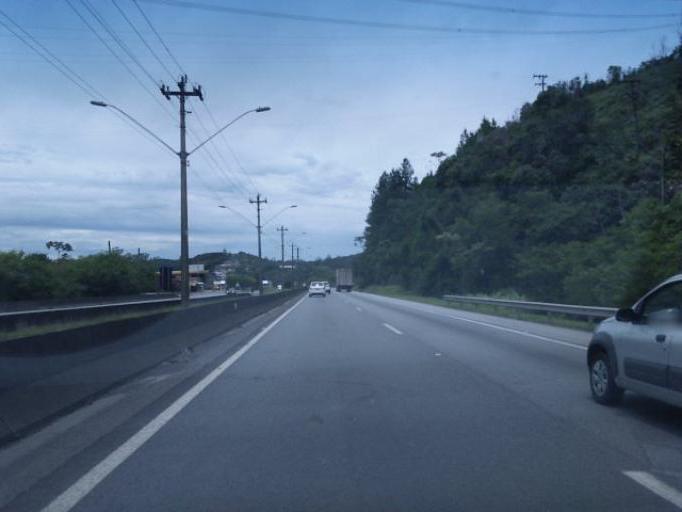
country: BR
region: Sao Paulo
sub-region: Sao Lourenco Da Serra
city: Sao Lourenco da Serra
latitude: -23.8890
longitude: -46.9802
